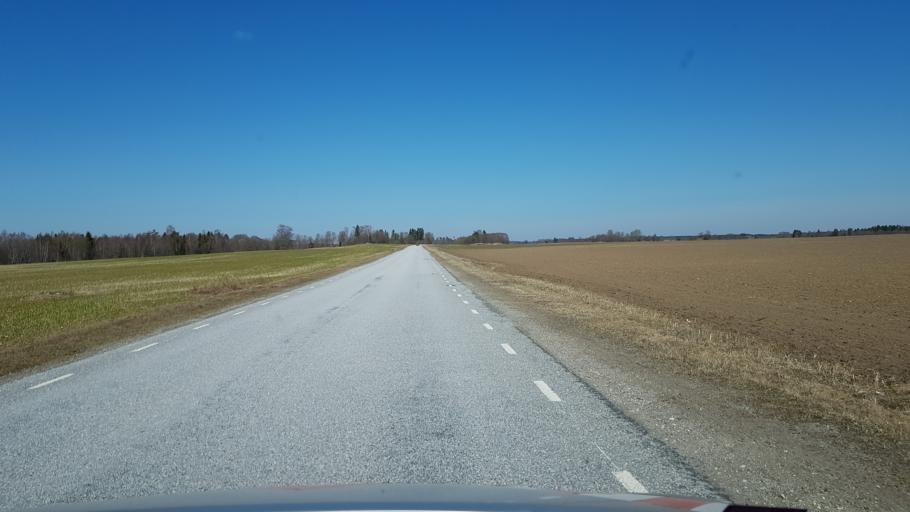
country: EE
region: Jaervamaa
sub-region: Koeru vald
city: Koeru
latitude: 59.0085
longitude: 26.0896
